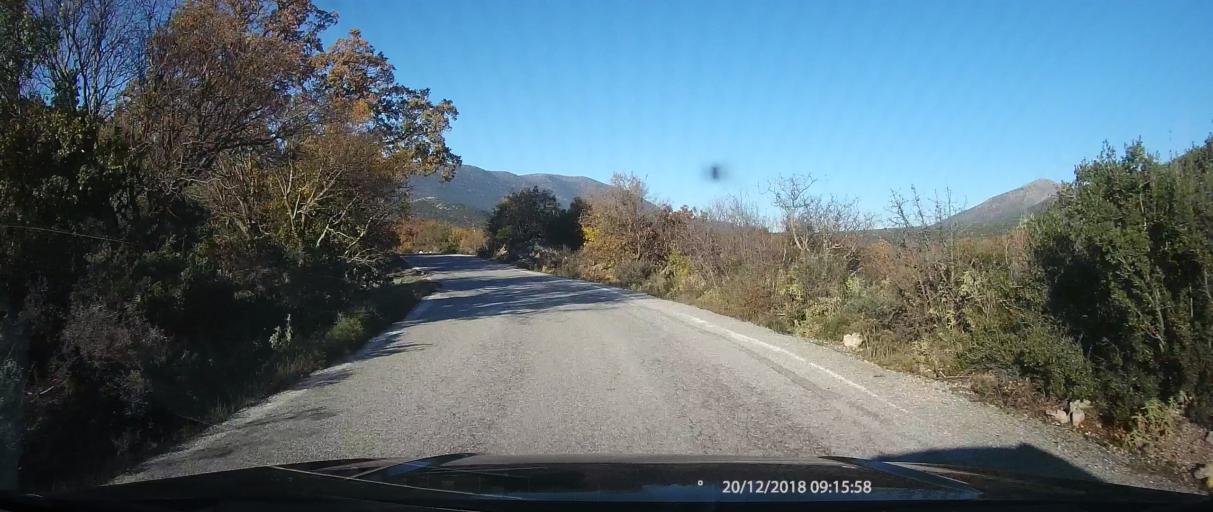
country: GR
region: Peloponnese
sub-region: Nomos Lakonias
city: Sykea
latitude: 36.9018
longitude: 22.9730
